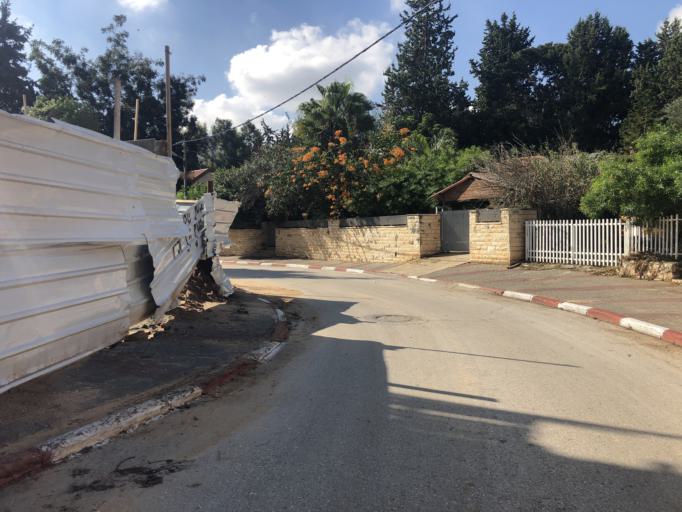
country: IL
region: Tel Aviv
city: Or Yehuda
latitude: 32.0291
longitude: 34.8683
